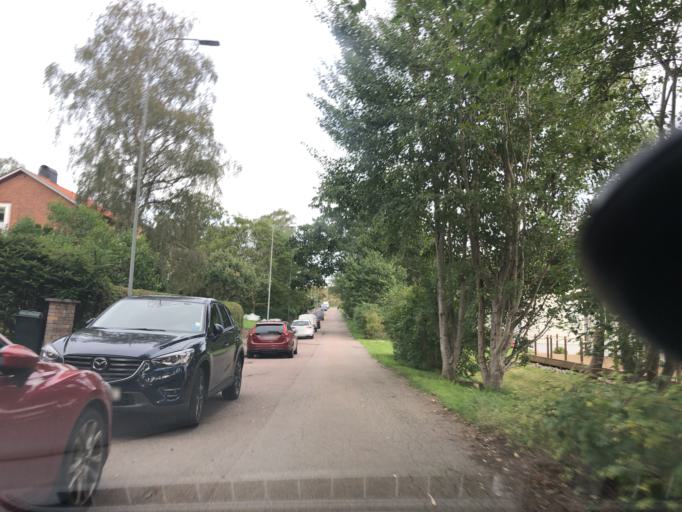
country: SE
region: Vaestra Goetaland
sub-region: Goteborg
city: Goeteborg
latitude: 57.7528
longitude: 11.9631
